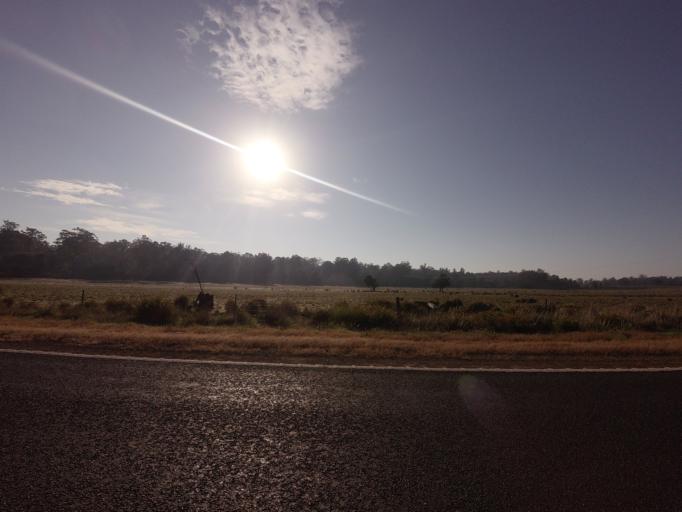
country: AU
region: Tasmania
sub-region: Northern Midlands
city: Longford
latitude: -41.5316
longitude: 147.0404
